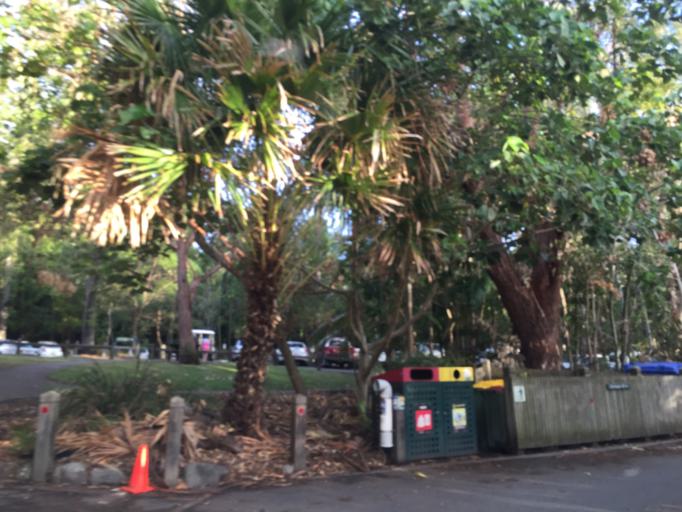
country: AU
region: Queensland
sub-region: Sunshine Coast
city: Noosa Heads
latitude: -26.3816
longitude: 153.0989
